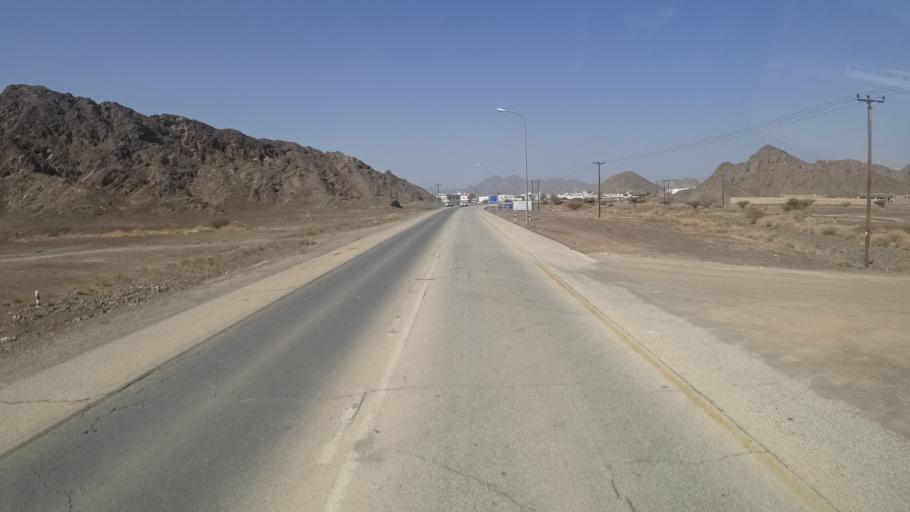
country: OM
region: Ash Sharqiyah
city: Ibra'
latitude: 22.6835
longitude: 58.5602
